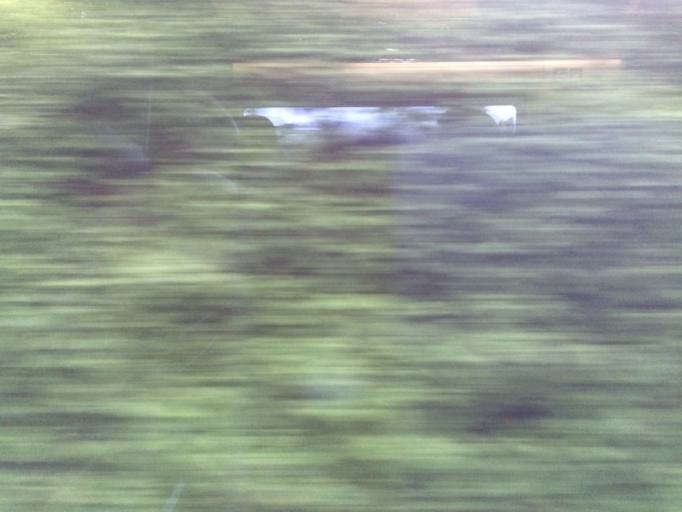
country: DE
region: Hesse
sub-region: Regierungsbezirk Darmstadt
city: Frankfurt am Main
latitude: 50.0800
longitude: 8.6694
